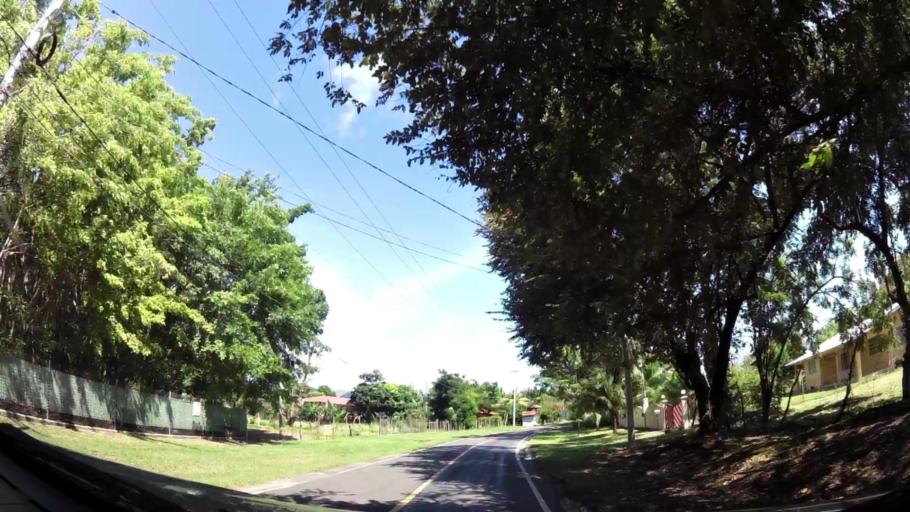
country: PA
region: Panama
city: Nueva Gorgona
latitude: 8.5597
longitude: -79.8829
